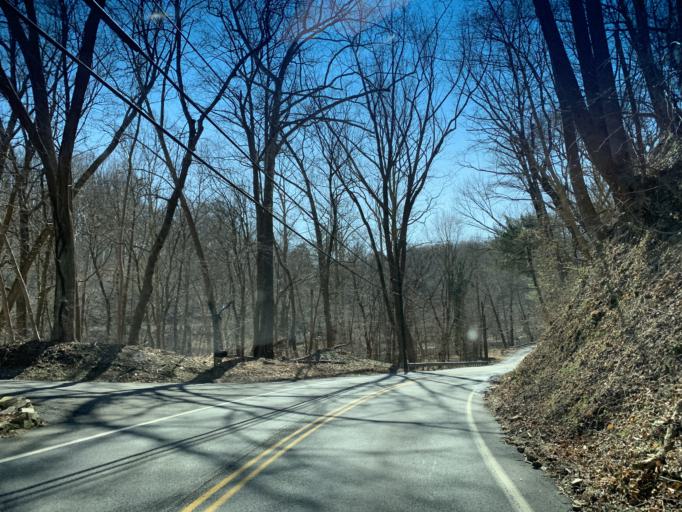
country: US
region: Maryland
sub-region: Cecil County
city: Rising Sun
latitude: 39.6645
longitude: -76.1475
